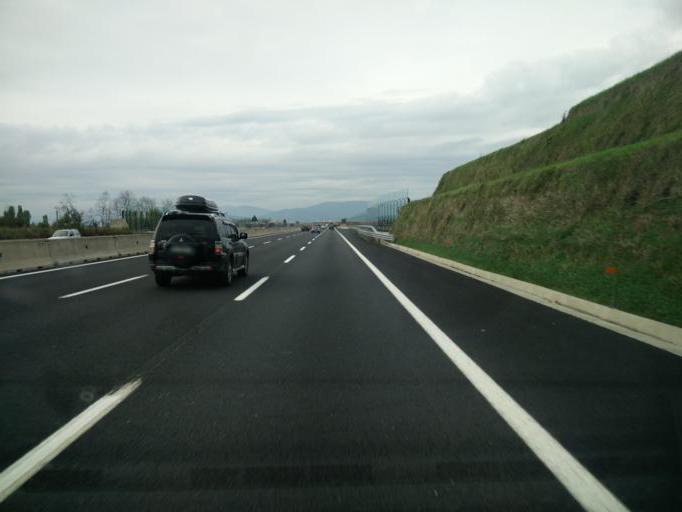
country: IT
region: Tuscany
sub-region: Province of Florence
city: Scandicci
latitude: 43.7497
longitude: 11.1720
